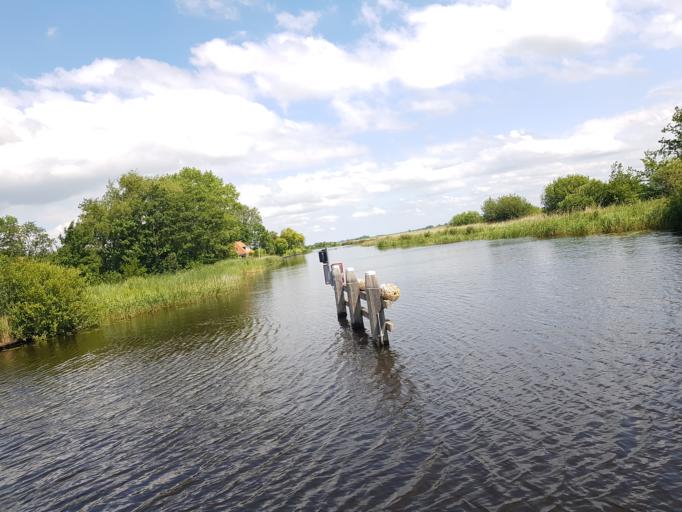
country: NL
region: Friesland
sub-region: Gemeente Boarnsterhim
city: Aldeboarn
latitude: 53.0923
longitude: 5.9072
